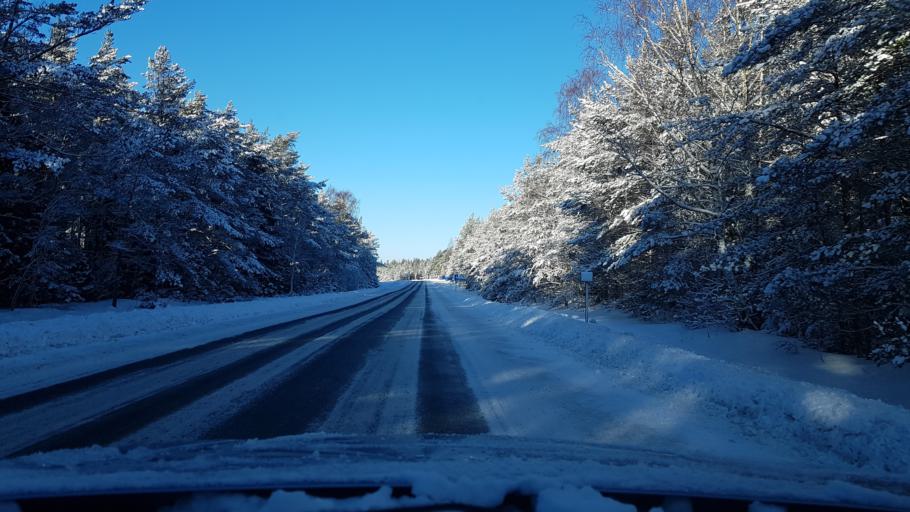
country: EE
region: Hiiumaa
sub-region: Kaerdla linn
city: Kardla
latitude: 58.9872
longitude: 22.7946
